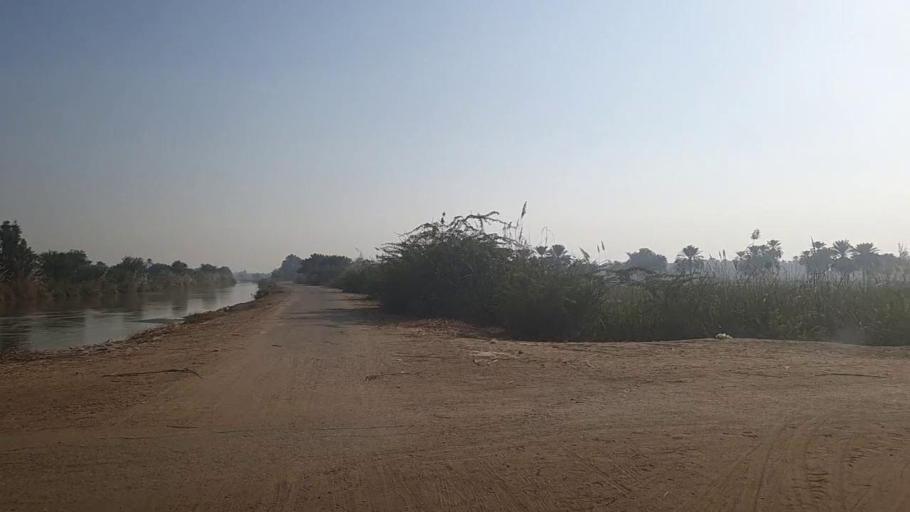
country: PK
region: Sindh
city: Bozdar
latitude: 27.2492
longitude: 68.6775
